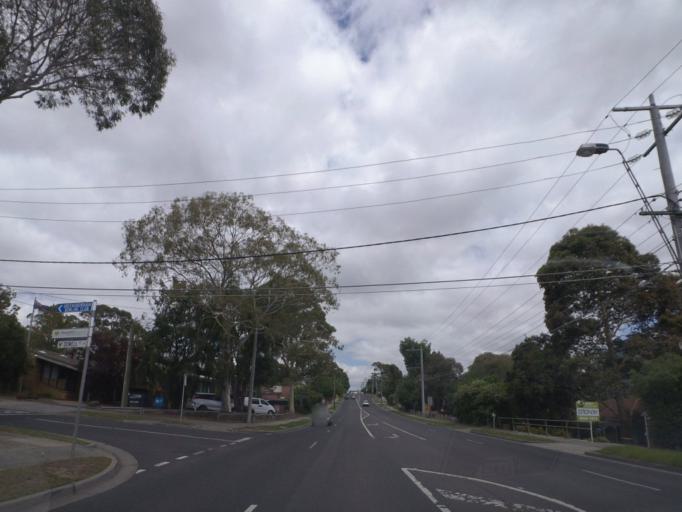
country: AU
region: Victoria
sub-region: Banyule
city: Greensborough
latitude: -37.7040
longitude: 145.0973
